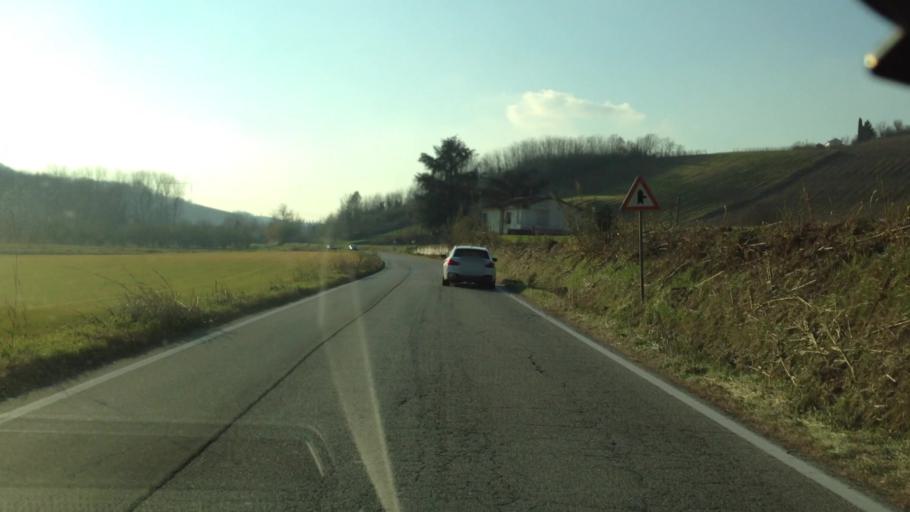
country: IT
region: Piedmont
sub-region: Provincia di Asti
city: Belveglio
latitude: 44.8330
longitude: 8.3433
